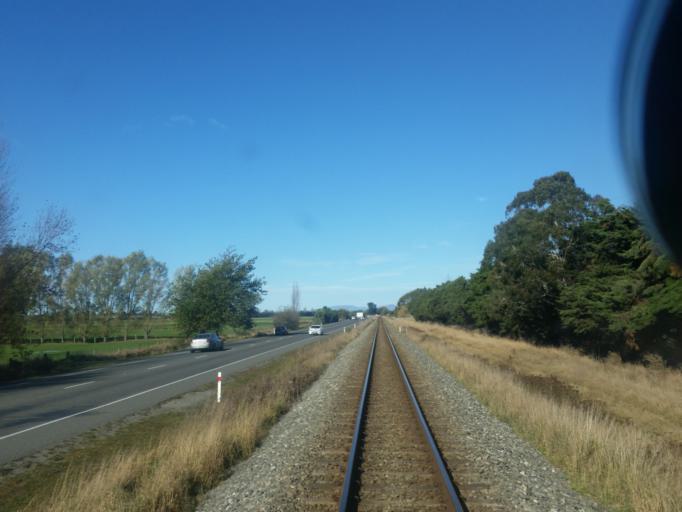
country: NZ
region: Canterbury
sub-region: Waimakariri District
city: Kaiapoi
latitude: -43.3601
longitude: 172.6312
